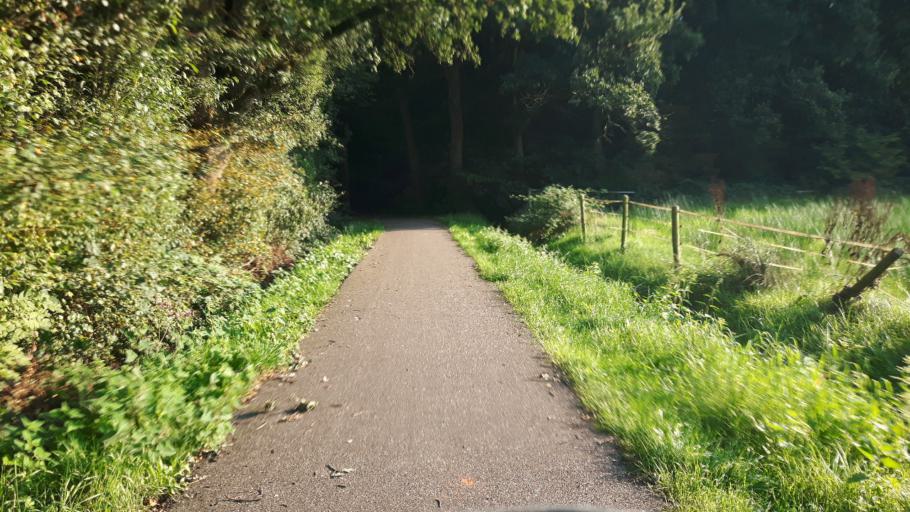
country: NL
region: Groningen
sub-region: Gemeente Leek
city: Leek
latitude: 53.1372
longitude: 6.4478
